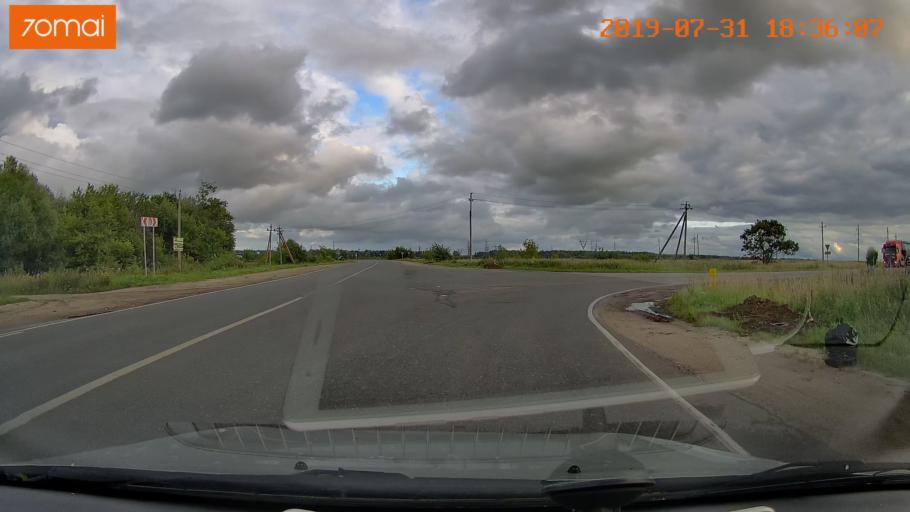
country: RU
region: Moskovskaya
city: Voskresensk
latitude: 55.2905
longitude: 38.6761
